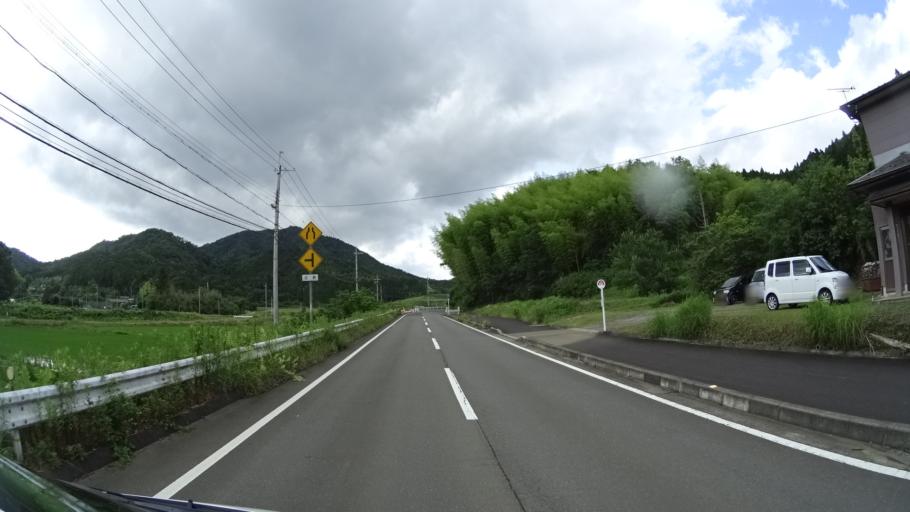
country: JP
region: Kyoto
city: Ayabe
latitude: 35.3327
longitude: 135.2056
